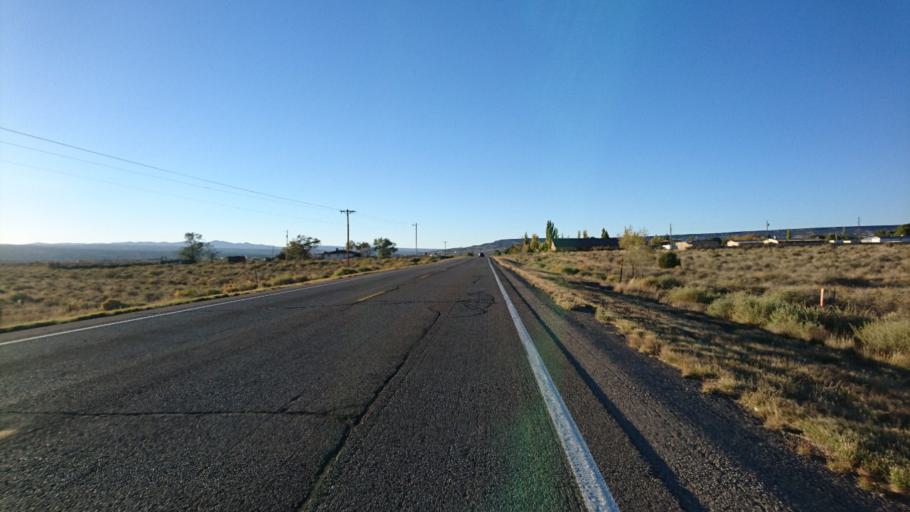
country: US
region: New Mexico
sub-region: Cibola County
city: Grants
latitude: 35.1258
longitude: -107.8029
